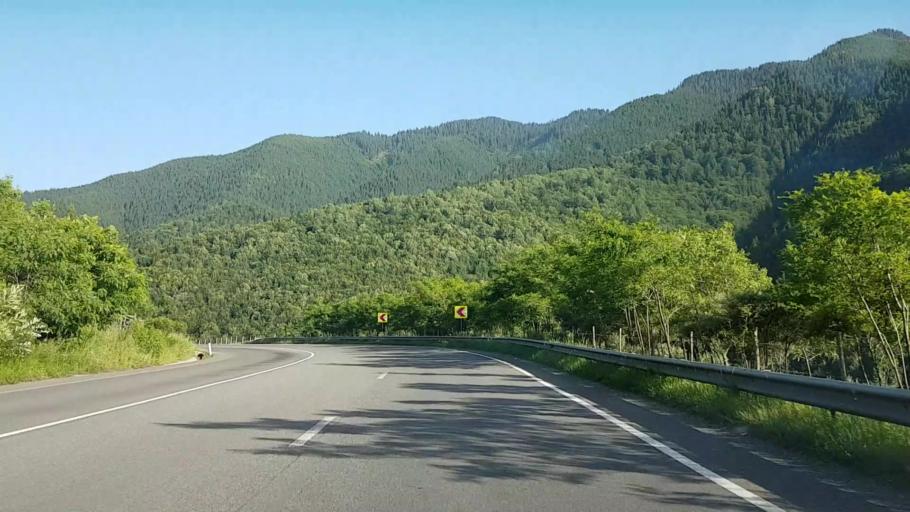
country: RO
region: Bistrita-Nasaud
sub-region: Comuna Tiha Bargaului
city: Tureac
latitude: 47.2225
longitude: 24.9294
